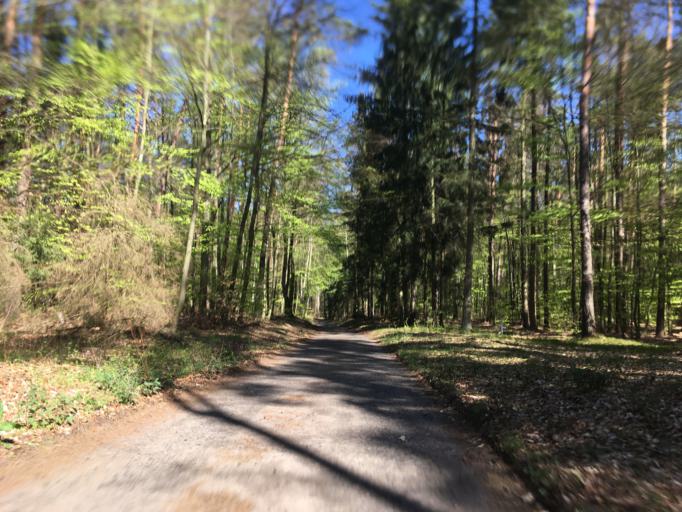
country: DE
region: Brandenburg
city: Wandlitz
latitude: 52.7500
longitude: 13.5367
